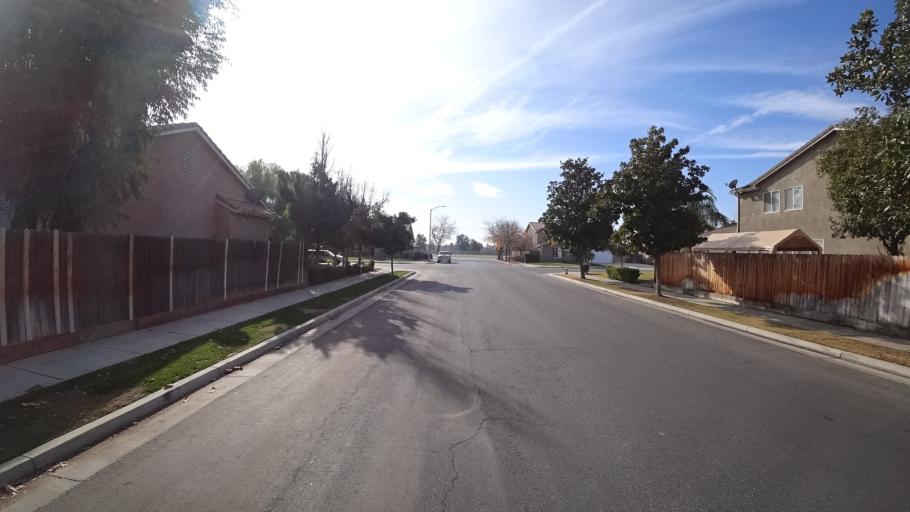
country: US
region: California
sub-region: Kern County
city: Rosedale
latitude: 35.4062
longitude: -119.1311
